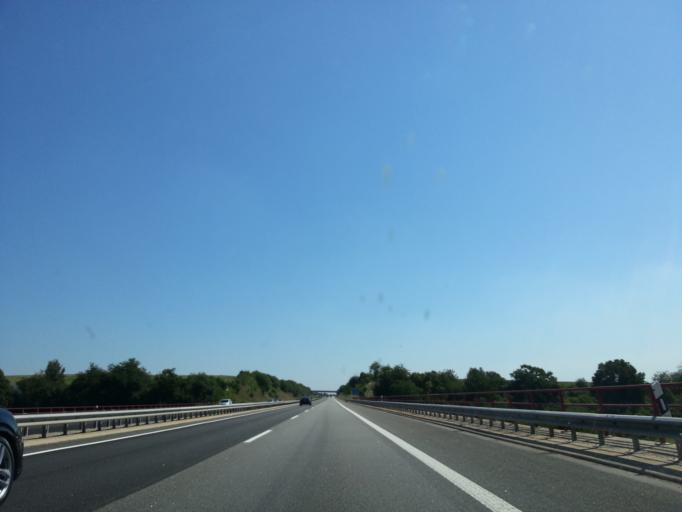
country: DE
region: Rheinland-Pfalz
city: Orsfeld
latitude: 50.0188
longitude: 6.6202
